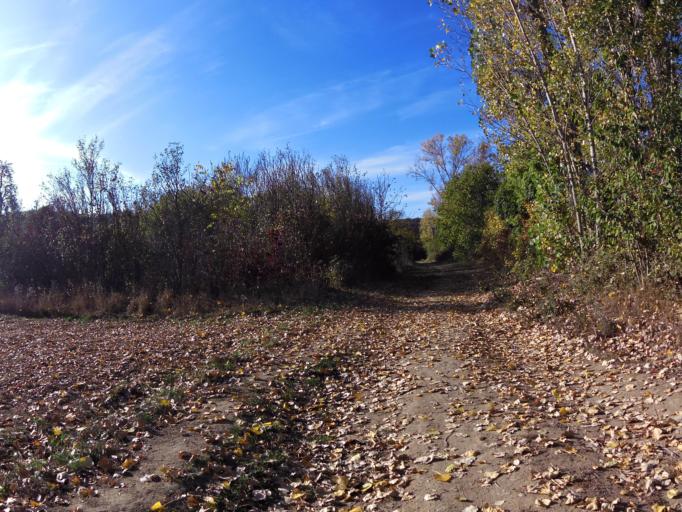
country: DE
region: Bavaria
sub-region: Regierungsbezirk Unterfranken
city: Eibelstadt
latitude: 49.7189
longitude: 10.0010
